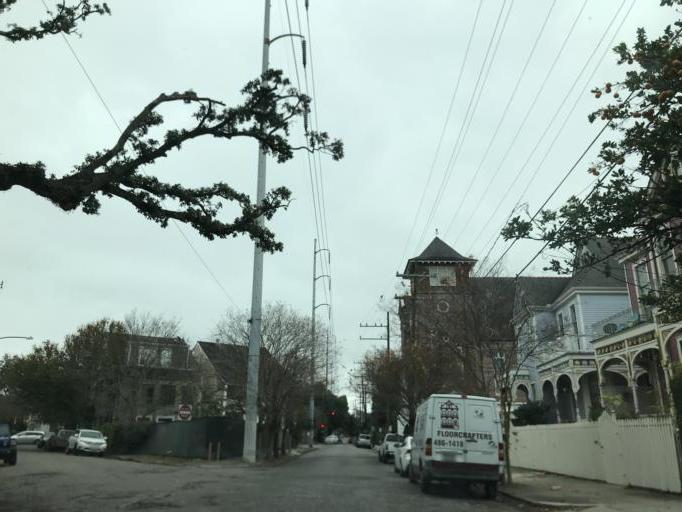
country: US
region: Louisiana
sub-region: Orleans Parish
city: New Orleans
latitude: 29.9340
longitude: -90.0751
